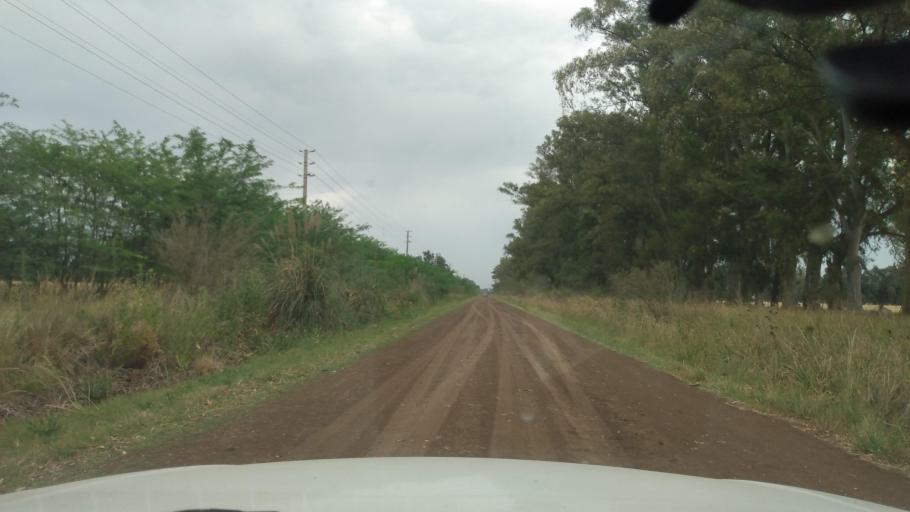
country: AR
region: Buenos Aires
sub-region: Partido de Lujan
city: Lujan
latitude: -34.5511
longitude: -59.1695
